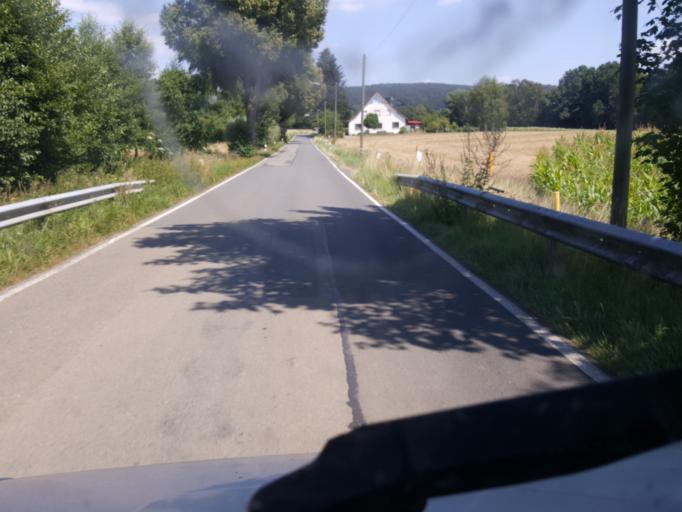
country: DE
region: North Rhine-Westphalia
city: Bad Oeynhausen
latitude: 52.2593
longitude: 8.7595
